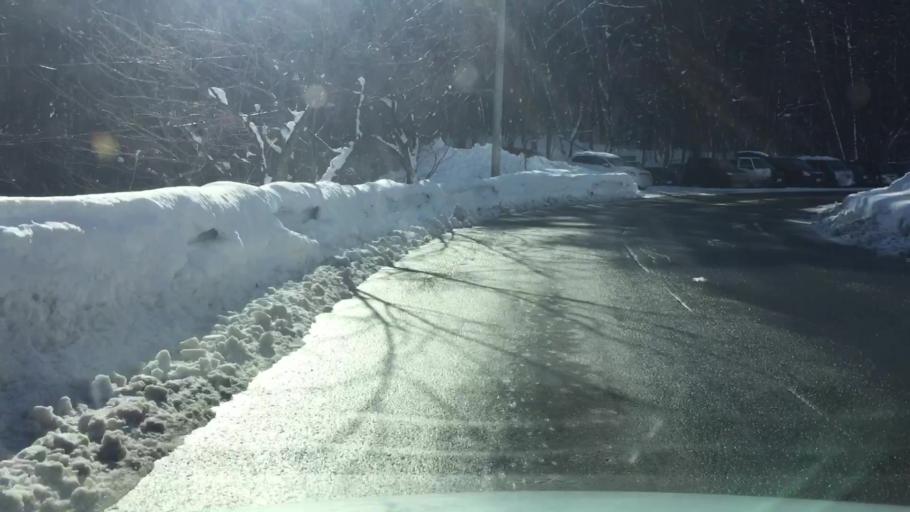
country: JP
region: Gunma
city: Numata
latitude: 36.7439
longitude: 138.9438
